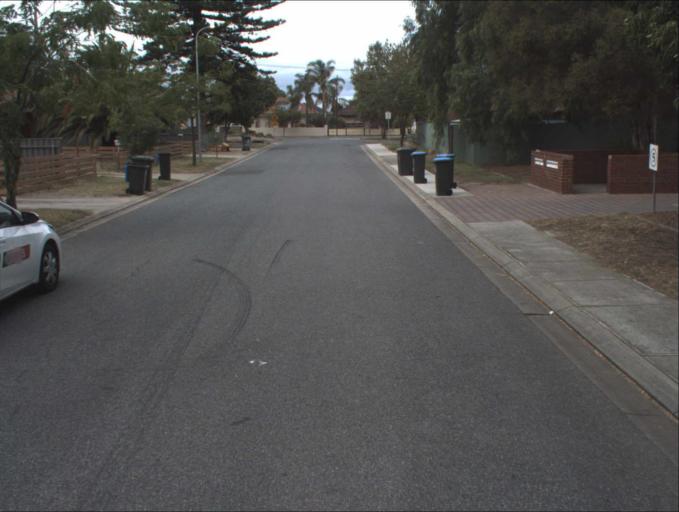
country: AU
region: South Australia
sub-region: Port Adelaide Enfield
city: Birkenhead
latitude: -34.8112
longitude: 138.4983
